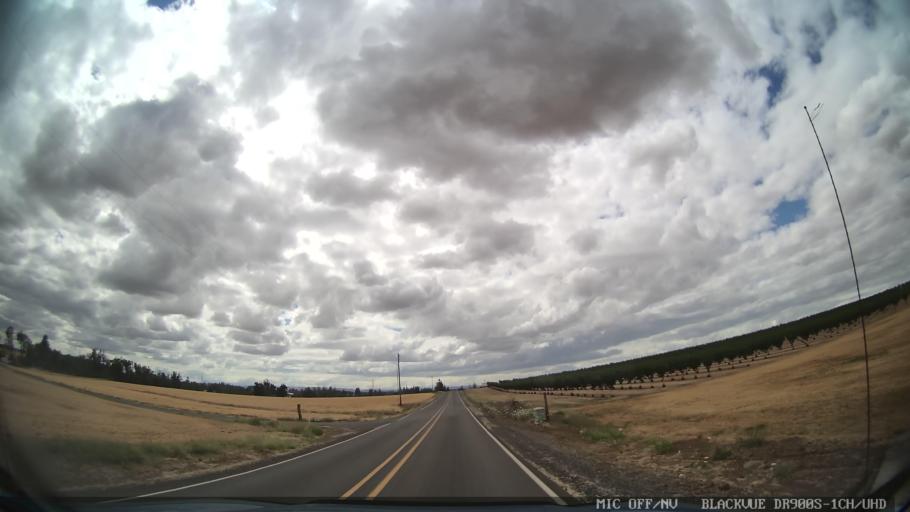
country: US
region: Oregon
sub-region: Marion County
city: Sublimity
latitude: 44.8443
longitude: -122.7567
